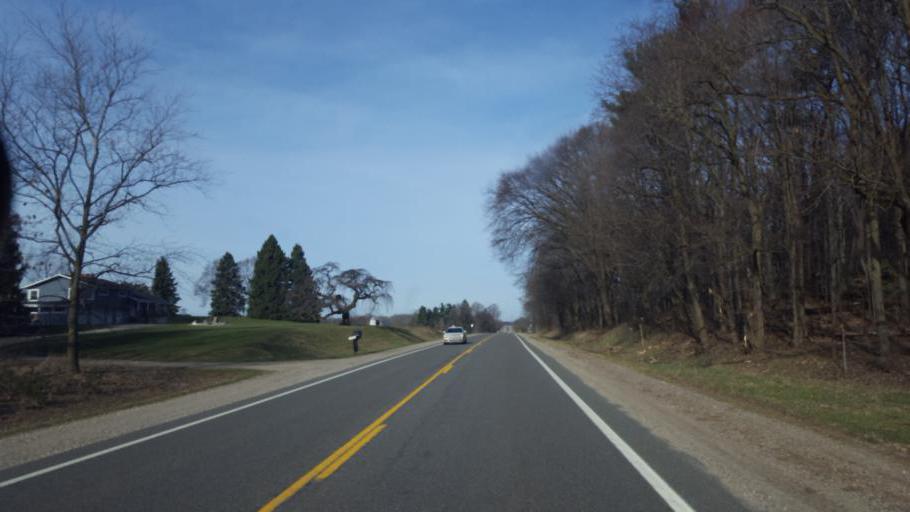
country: US
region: Michigan
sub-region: Montcalm County
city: Lakeview
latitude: 43.4322
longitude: -85.3428
